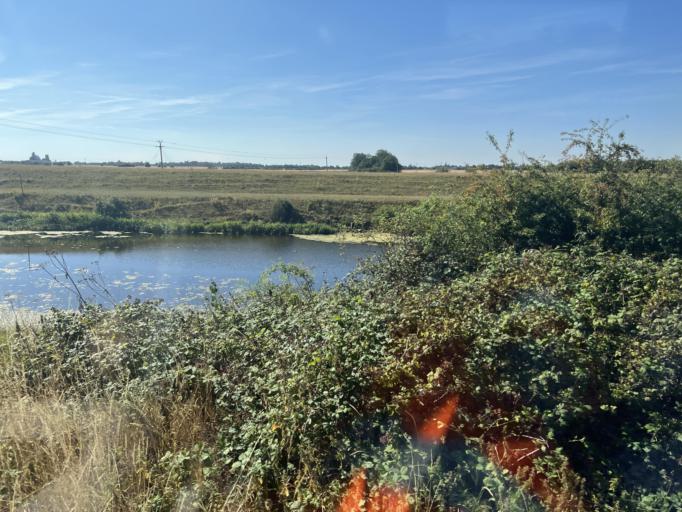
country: GB
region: England
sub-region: Lincolnshire
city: Donington
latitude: 52.9730
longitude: -0.1607
